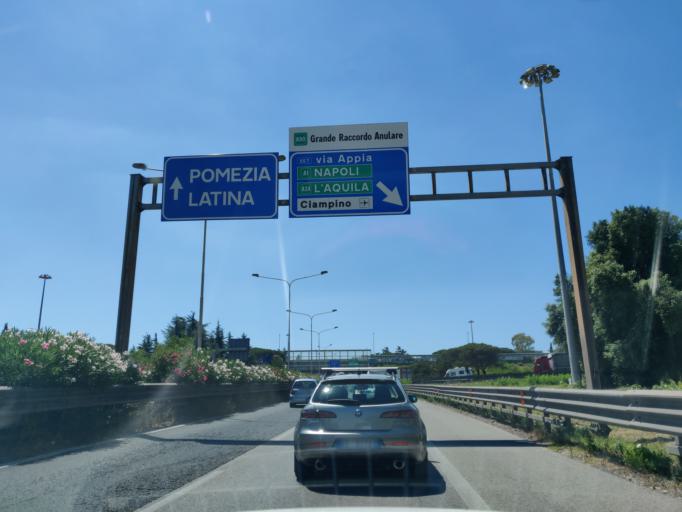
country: IT
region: Latium
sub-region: Citta metropolitana di Roma Capitale
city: Selcetta
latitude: 41.8029
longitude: 12.4540
